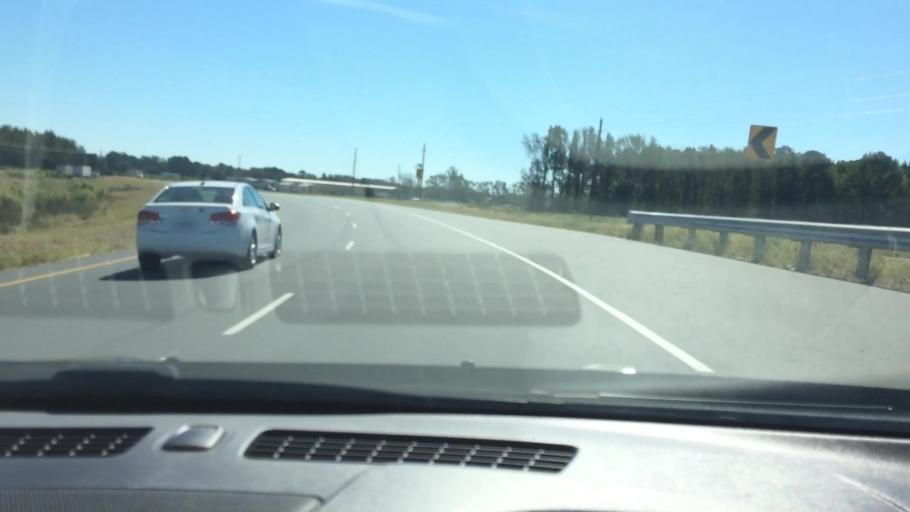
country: US
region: North Carolina
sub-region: Pitt County
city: Ayden
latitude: 35.4605
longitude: -77.4364
